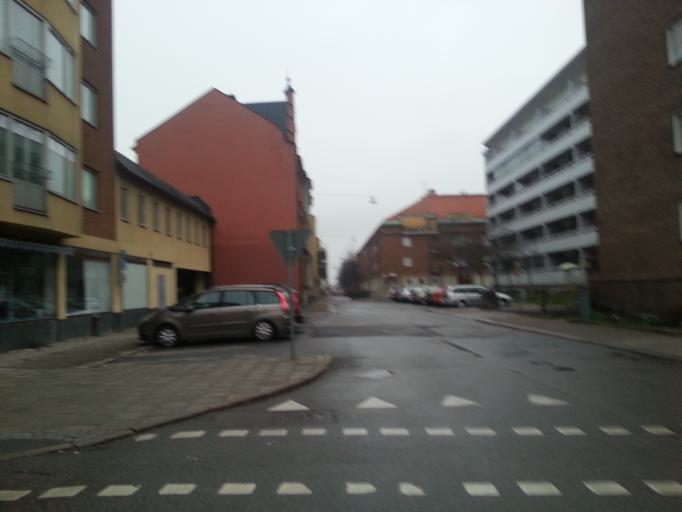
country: SE
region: OEstergoetland
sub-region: Norrkopings Kommun
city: Norrkoping
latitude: 58.5894
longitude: 16.1939
